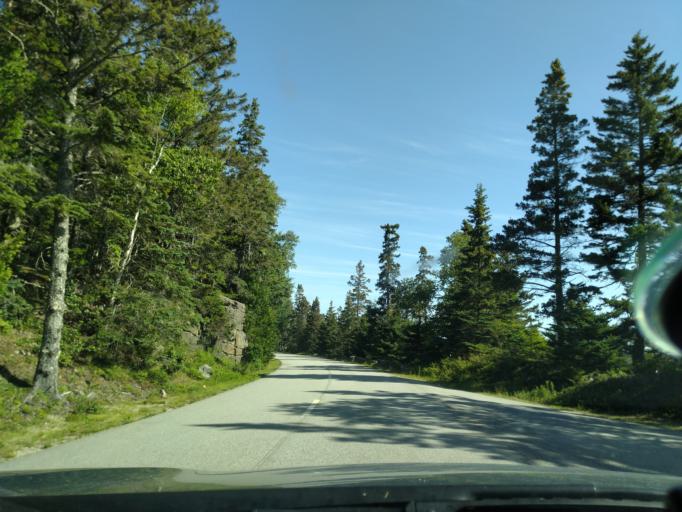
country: US
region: Maine
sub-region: Hancock County
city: Gouldsboro
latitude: 44.3419
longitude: -68.0442
